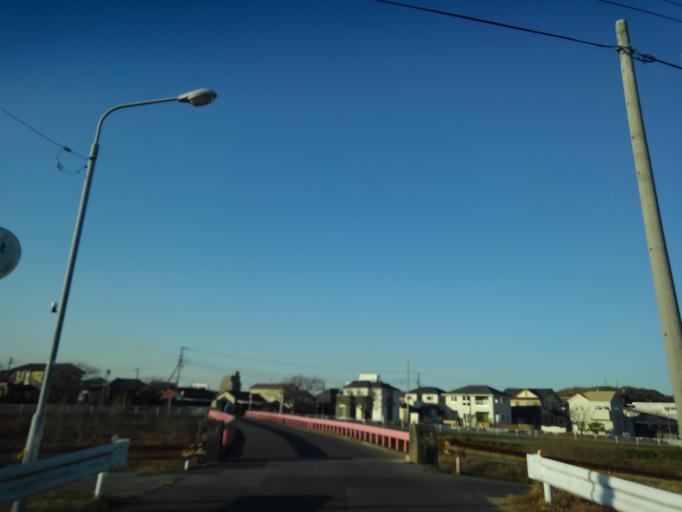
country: JP
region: Chiba
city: Kimitsu
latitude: 35.3243
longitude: 139.9043
